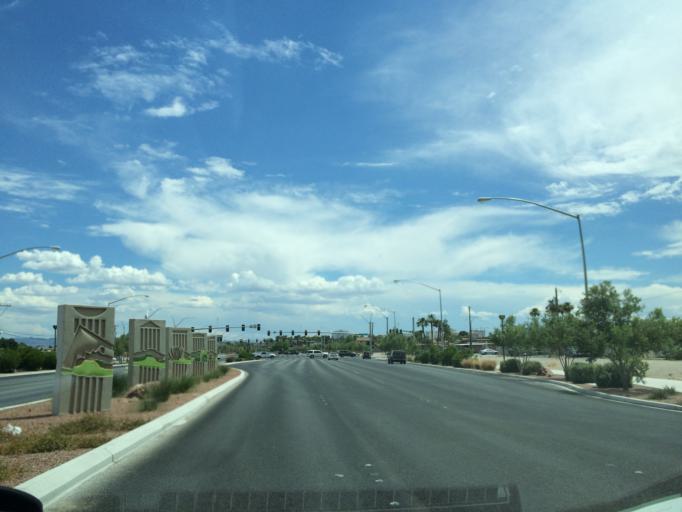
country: US
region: Nevada
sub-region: Clark County
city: North Las Vegas
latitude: 36.1983
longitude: -115.1339
